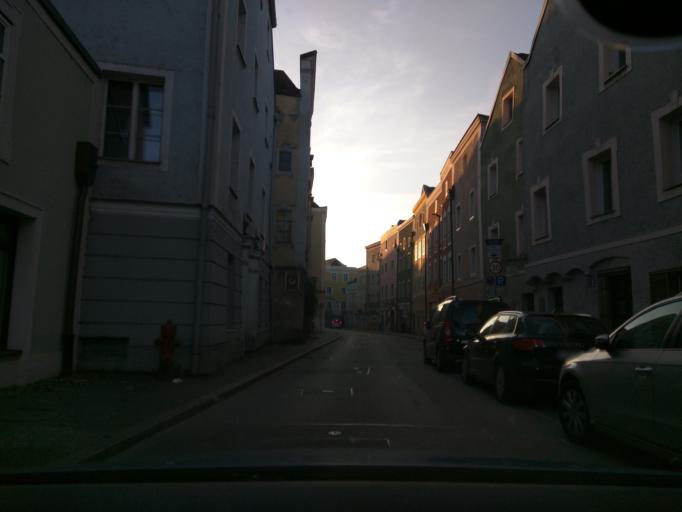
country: DE
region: Bavaria
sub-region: Lower Bavaria
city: Passau
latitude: 48.5709
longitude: 13.4681
